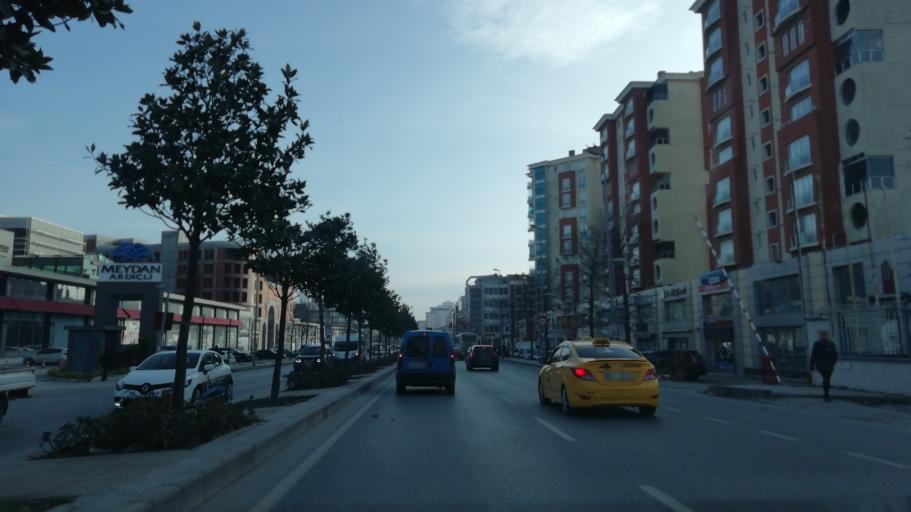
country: TR
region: Istanbul
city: Esenyurt
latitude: 41.0471
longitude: 28.6742
